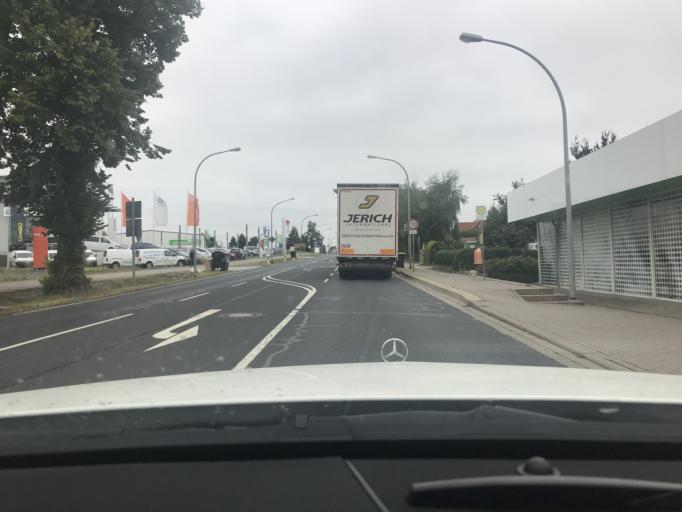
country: DE
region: Thuringia
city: Leinefelde
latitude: 51.3933
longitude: 10.3263
